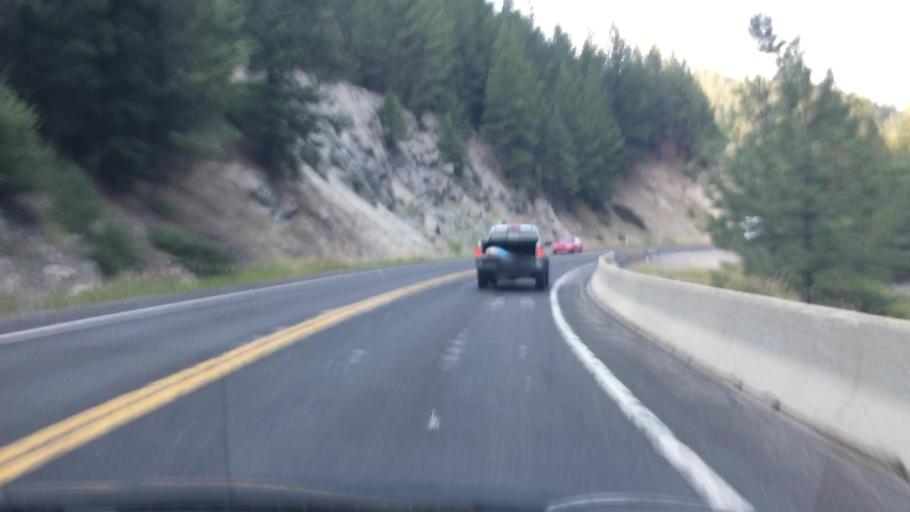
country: US
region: Idaho
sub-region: Valley County
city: Cascade
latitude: 44.2467
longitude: -116.0955
